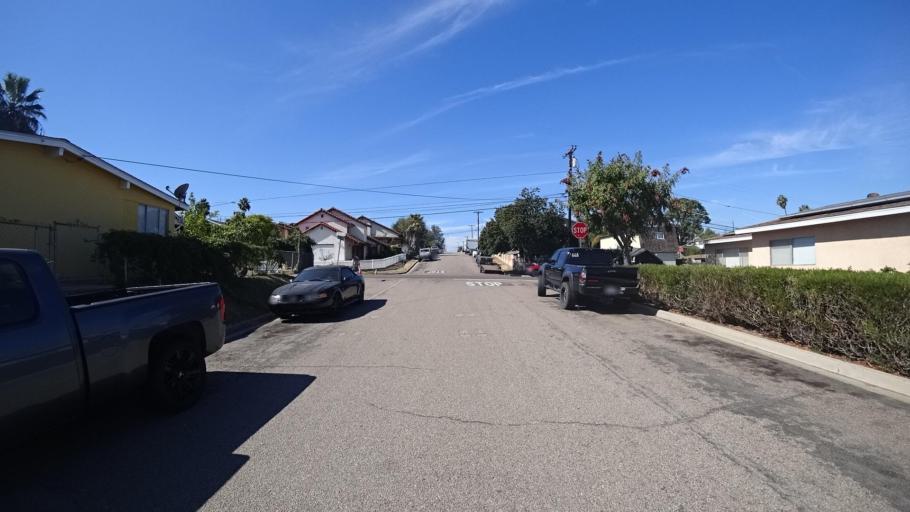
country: US
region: California
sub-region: San Diego County
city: La Presa
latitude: 32.7097
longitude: -116.9921
